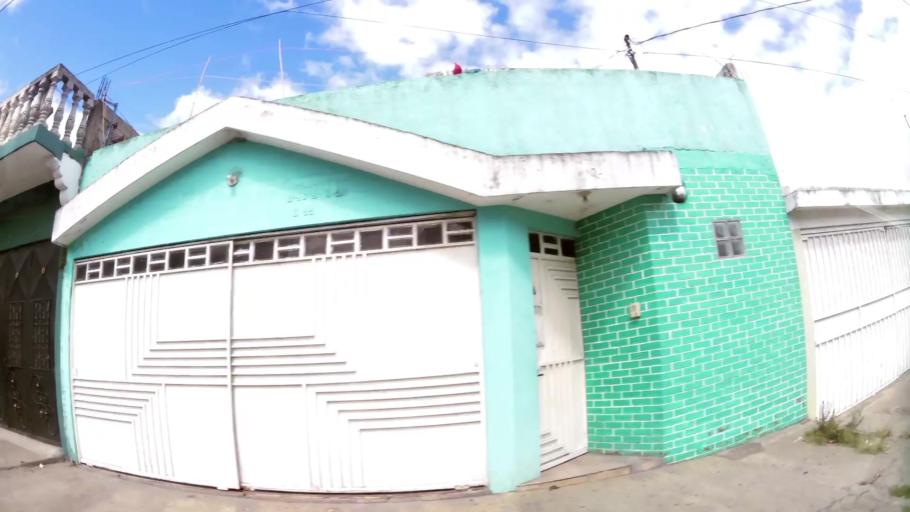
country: GT
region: Guatemala
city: Guatemala City
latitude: 14.6811
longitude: -90.5435
